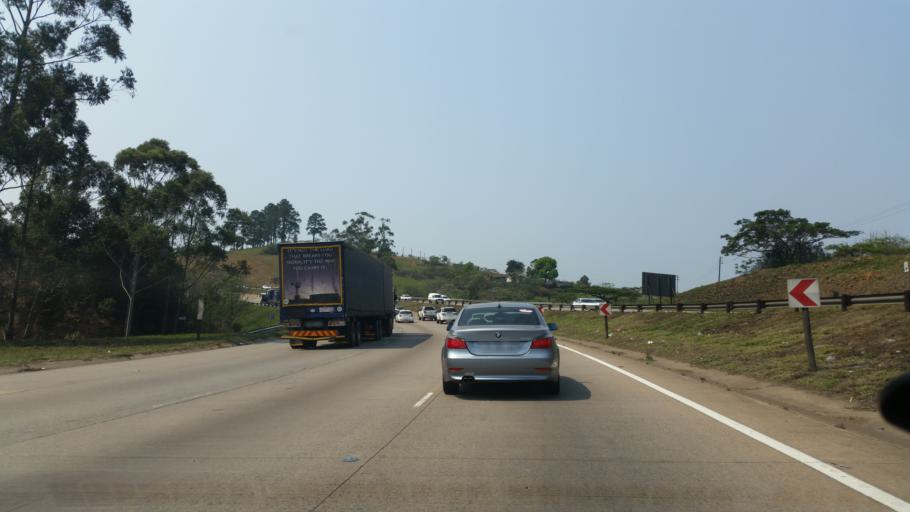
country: ZA
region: KwaZulu-Natal
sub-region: eThekwini Metropolitan Municipality
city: Mpumalanga
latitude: -29.7765
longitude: 30.6967
